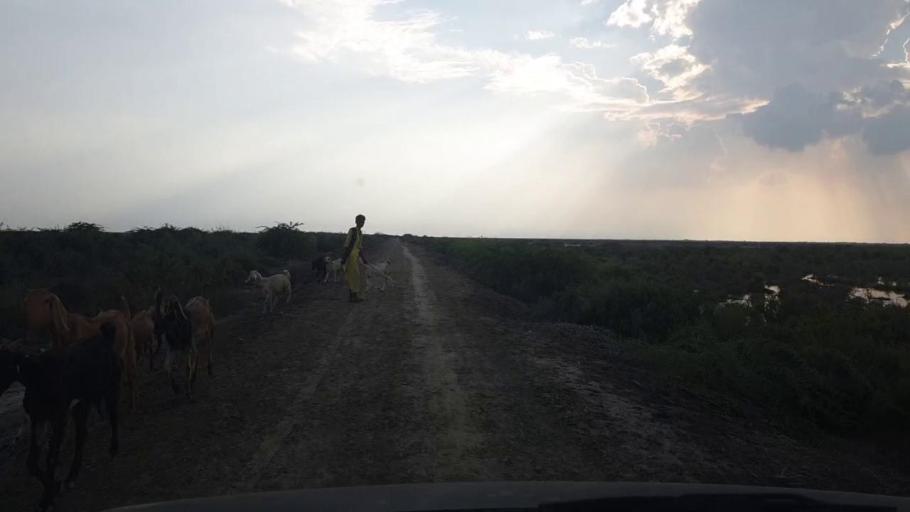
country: PK
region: Sindh
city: Badin
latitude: 24.4622
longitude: 68.6908
